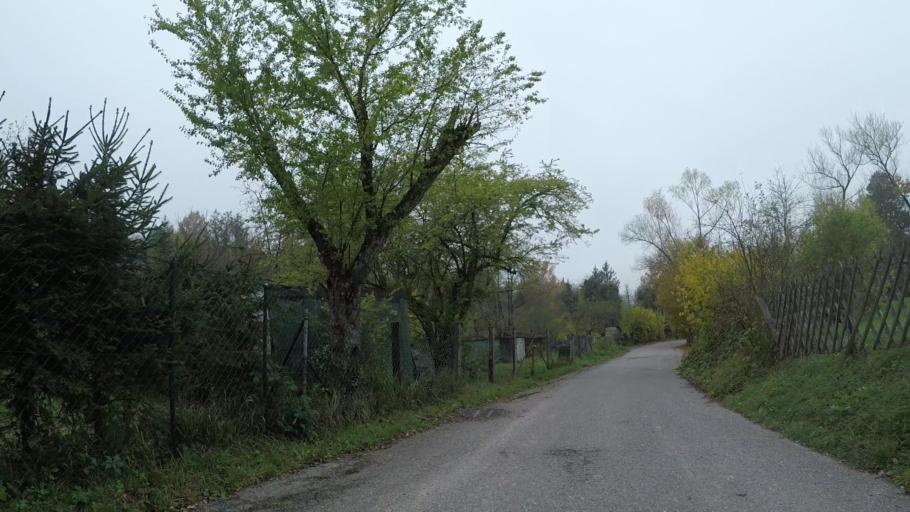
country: DE
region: Baden-Wuerttemberg
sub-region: Tuebingen Region
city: Eningen unter Achalm
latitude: 48.4869
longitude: 9.2388
